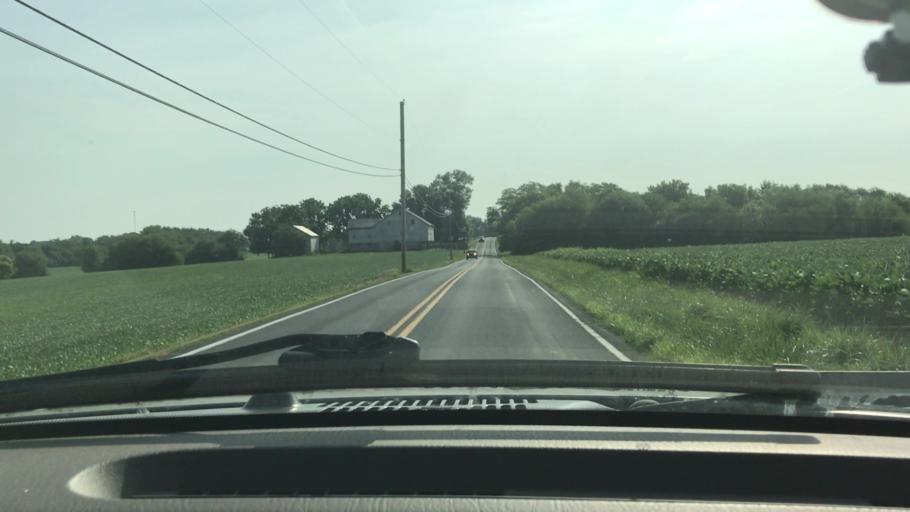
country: US
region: Pennsylvania
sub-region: Lancaster County
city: Rheems
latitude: 40.1388
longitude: -76.5803
